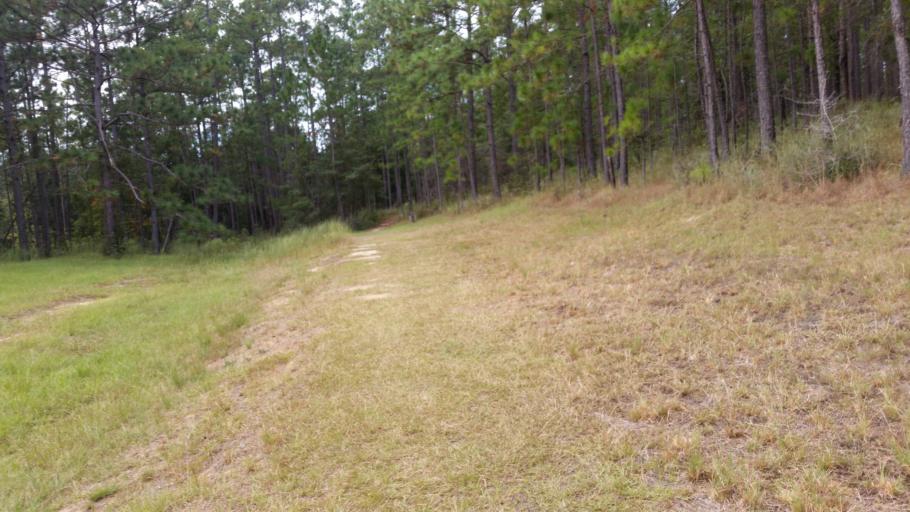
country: US
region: Florida
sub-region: Santa Rosa County
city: Point Baker
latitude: 30.8644
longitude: -86.8355
